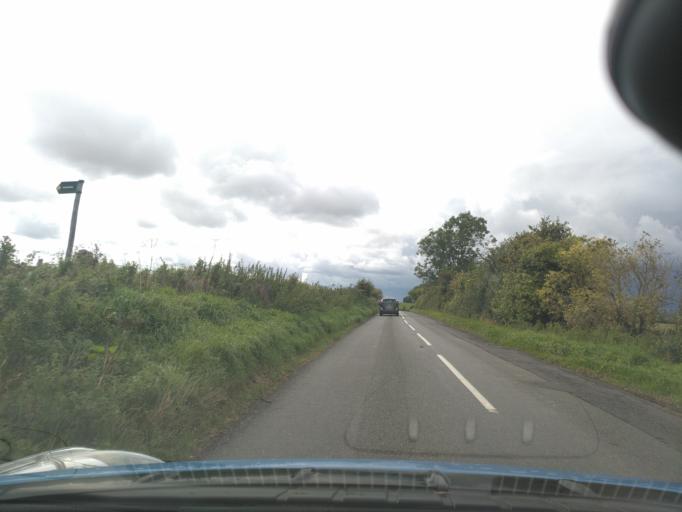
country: GB
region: England
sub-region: Oxfordshire
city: Stanford in the Vale
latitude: 51.5822
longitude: -1.5396
